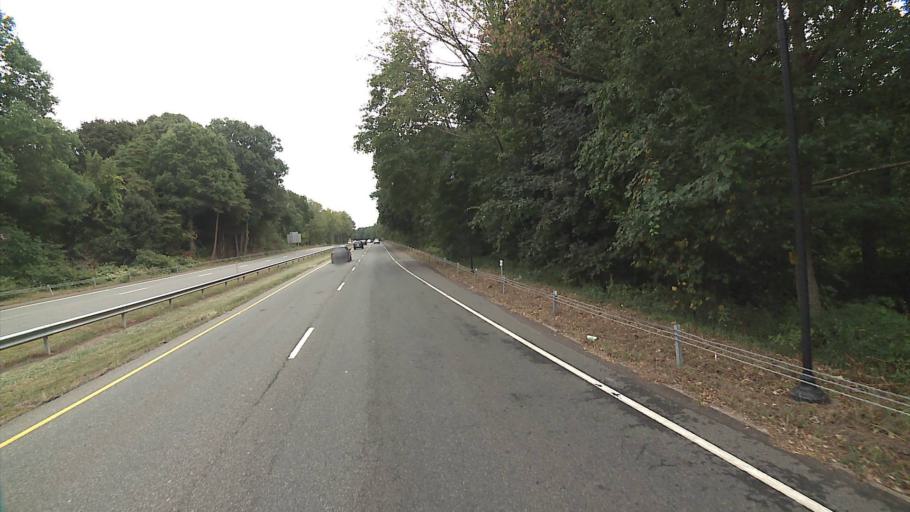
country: US
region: Connecticut
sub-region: New Haven County
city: North Haven
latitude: 41.3994
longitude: -72.8678
